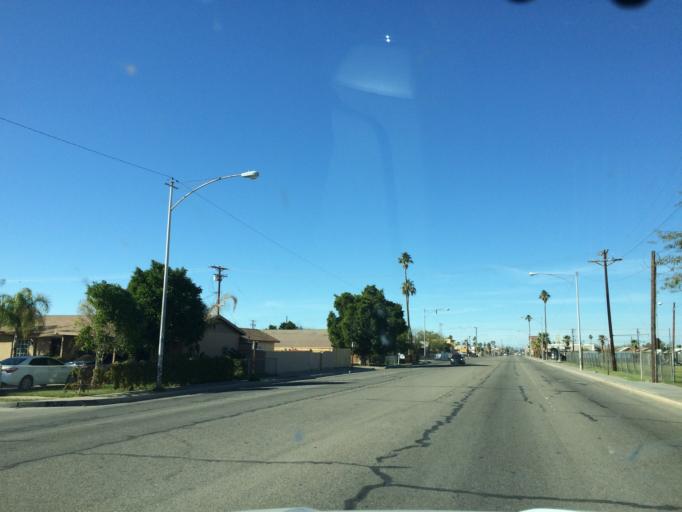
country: US
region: California
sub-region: Imperial County
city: El Centro
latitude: 32.7830
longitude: -115.5524
